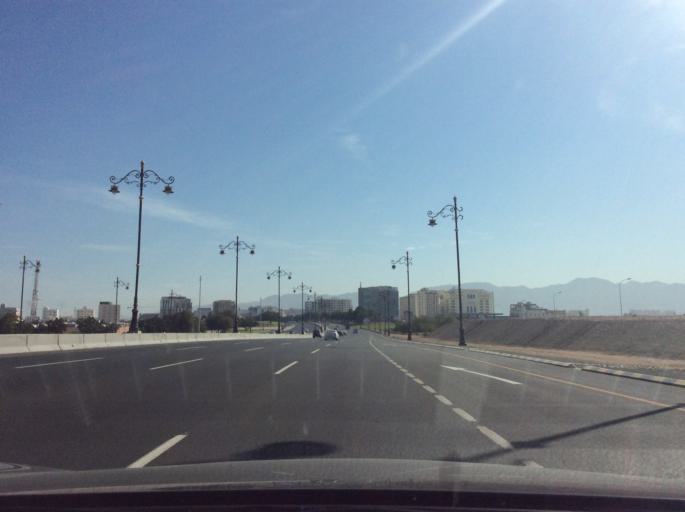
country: OM
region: Muhafazat Masqat
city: Bawshar
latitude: 23.5910
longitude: 58.3510
